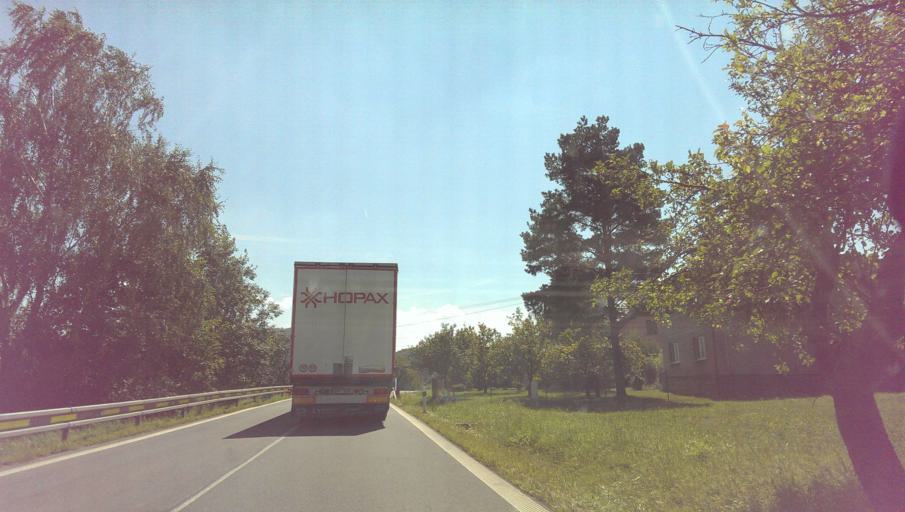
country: CZ
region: Moravskoslezsky
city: Koprivnice
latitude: 49.6013
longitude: 18.1805
